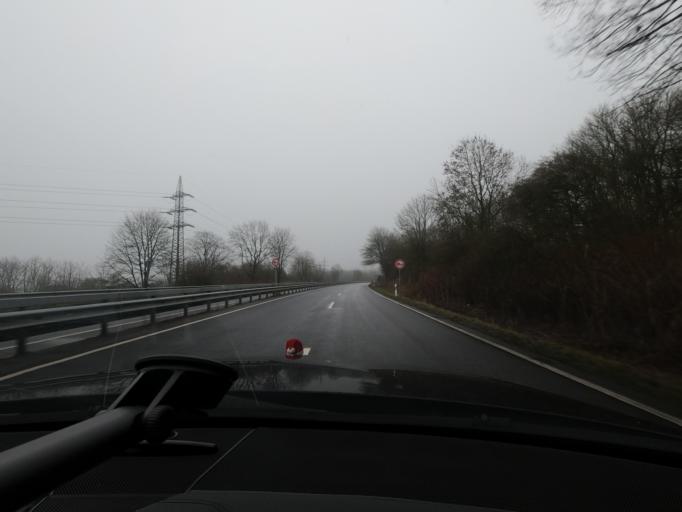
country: DE
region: Schleswig-Holstein
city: Harrislee
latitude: 54.8001
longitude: 9.4088
